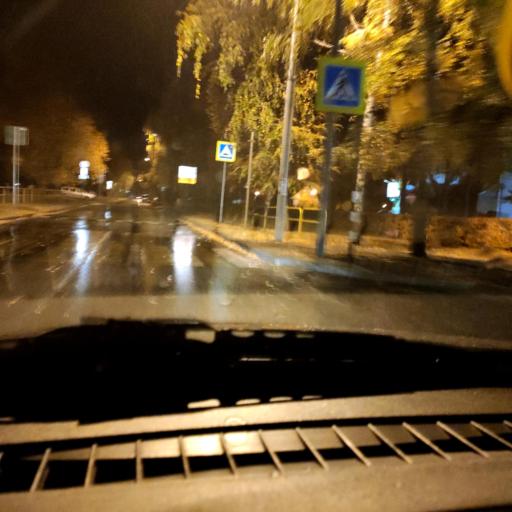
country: RU
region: Samara
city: Tol'yatti
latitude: 53.5095
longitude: 49.2837
